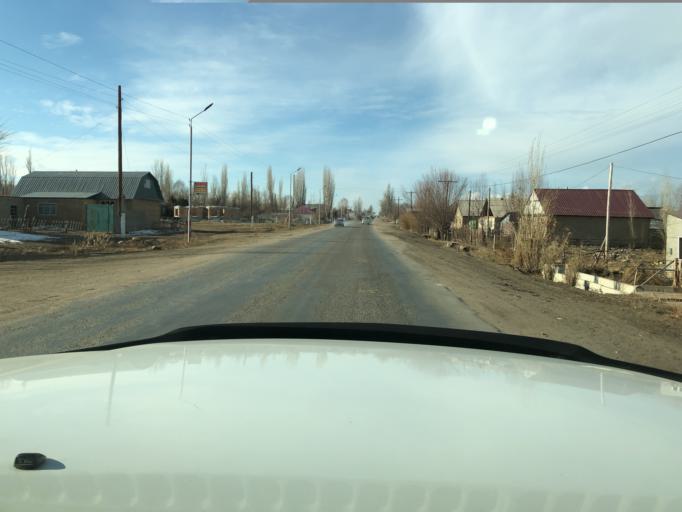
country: KG
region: Ysyk-Koel
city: Pokrovka
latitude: 42.3250
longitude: 77.9406
